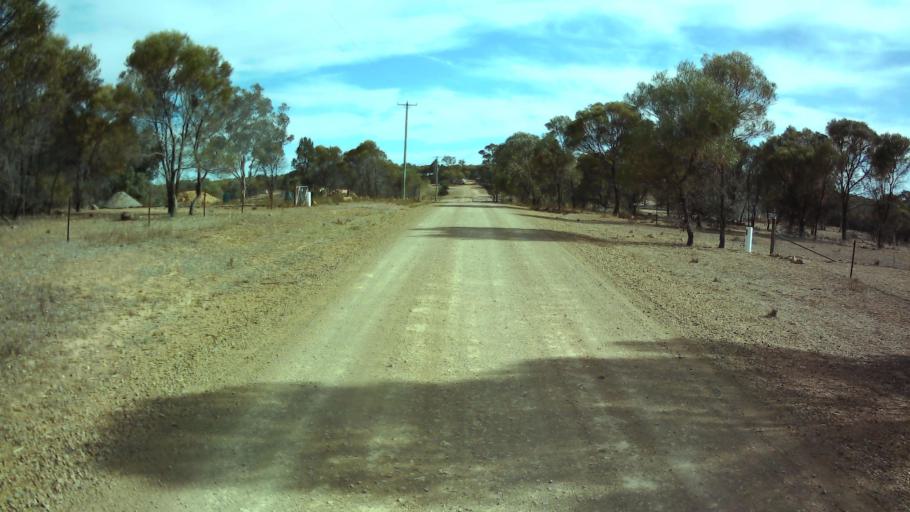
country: AU
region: New South Wales
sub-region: Weddin
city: Grenfell
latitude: -33.8718
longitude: 148.1921
